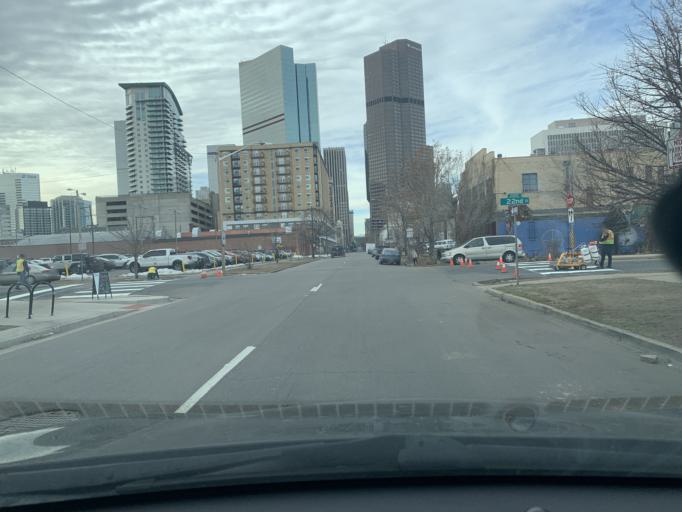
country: US
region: Colorado
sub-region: Denver County
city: Denver
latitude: 39.7510
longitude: -104.9847
